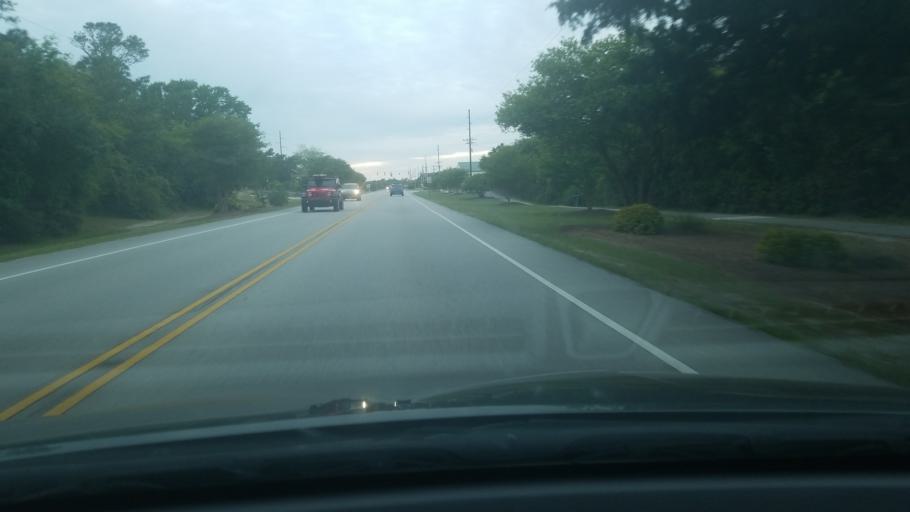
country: US
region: North Carolina
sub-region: Carteret County
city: Cape Carteret
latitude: 34.6624
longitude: -77.0462
